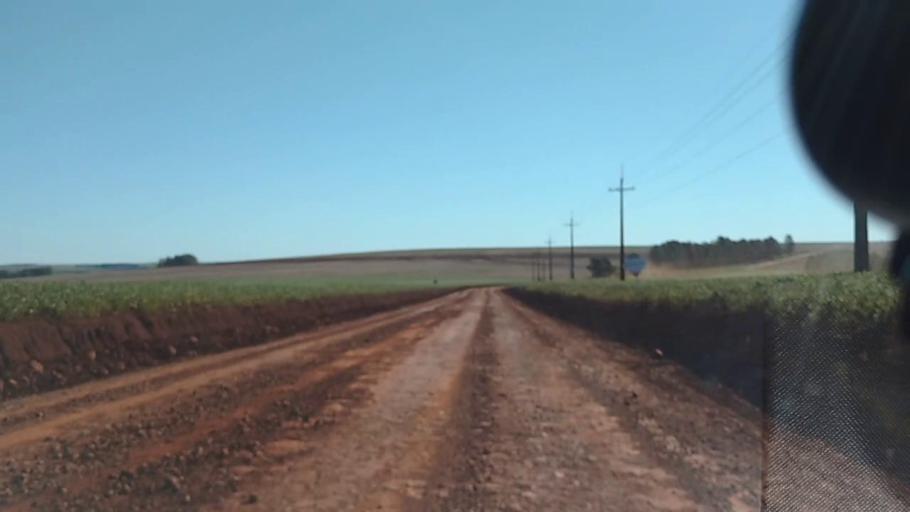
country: PY
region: Alto Parana
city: Naranjal
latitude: -25.9751
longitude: -55.2264
